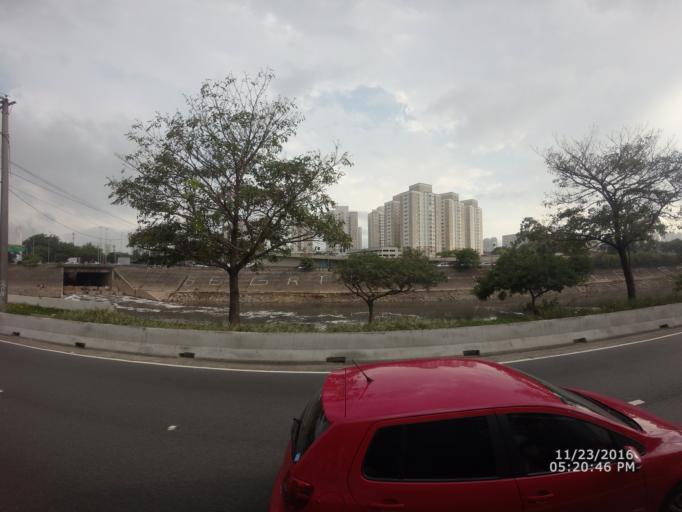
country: BR
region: Sao Paulo
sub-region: Guarulhos
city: Guarulhos
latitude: -23.5230
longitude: -46.5610
